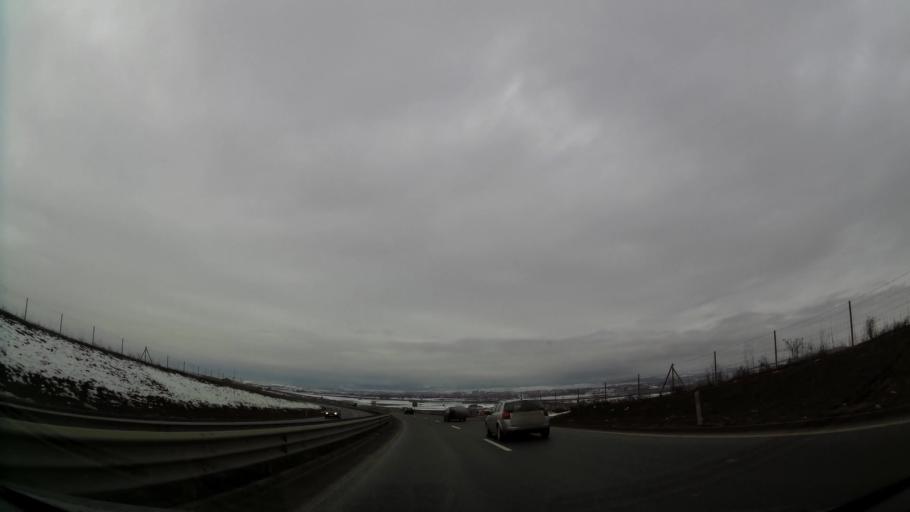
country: XK
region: Pristina
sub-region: Komuna e Prishtines
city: Pristina
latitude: 42.6322
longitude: 21.1409
